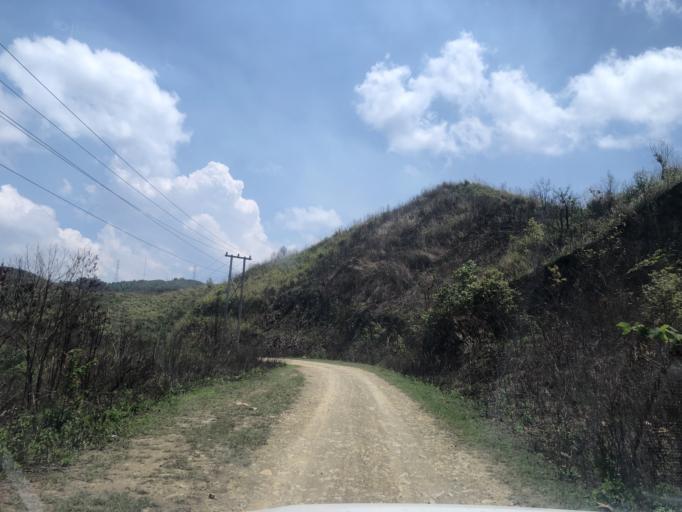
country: LA
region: Phongsali
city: Phongsali
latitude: 21.4050
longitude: 102.1857
